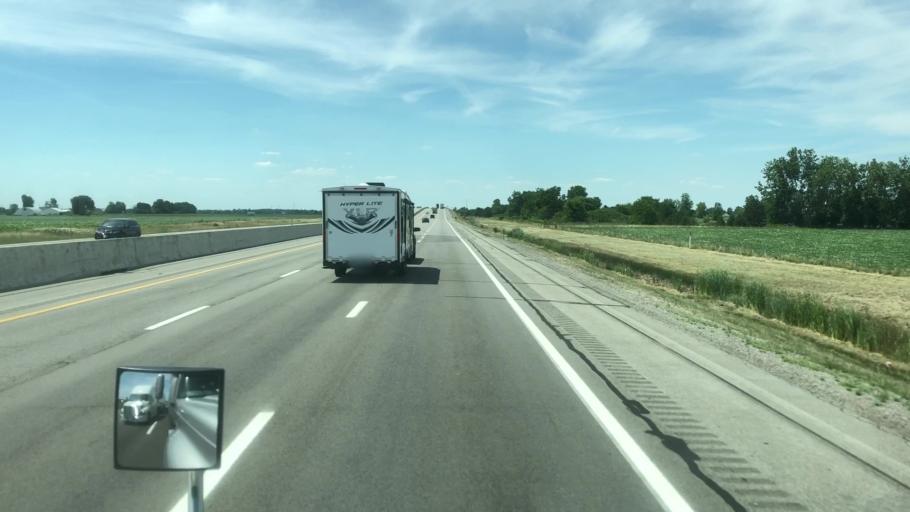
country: US
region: Ohio
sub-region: Wood County
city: Walbridge
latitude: 41.5386
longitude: -83.4994
